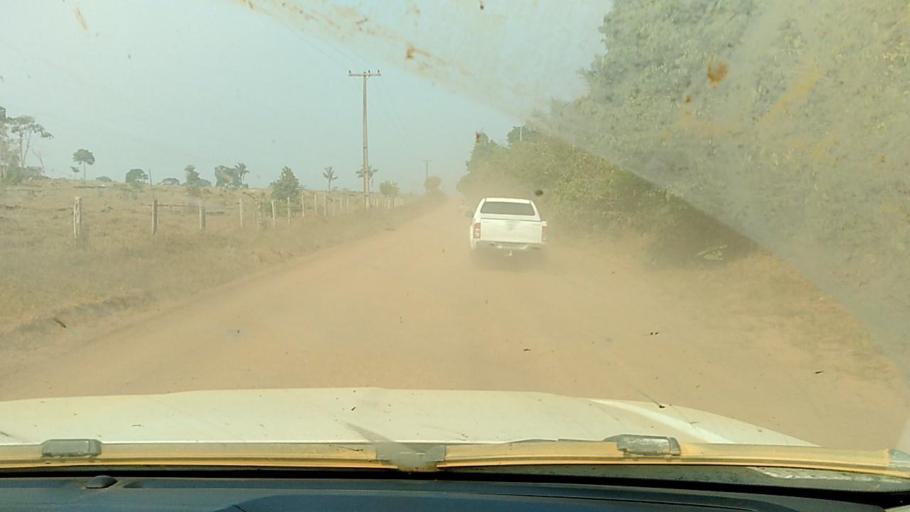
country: BR
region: Rondonia
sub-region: Porto Velho
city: Porto Velho
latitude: -8.8441
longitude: -64.1610
